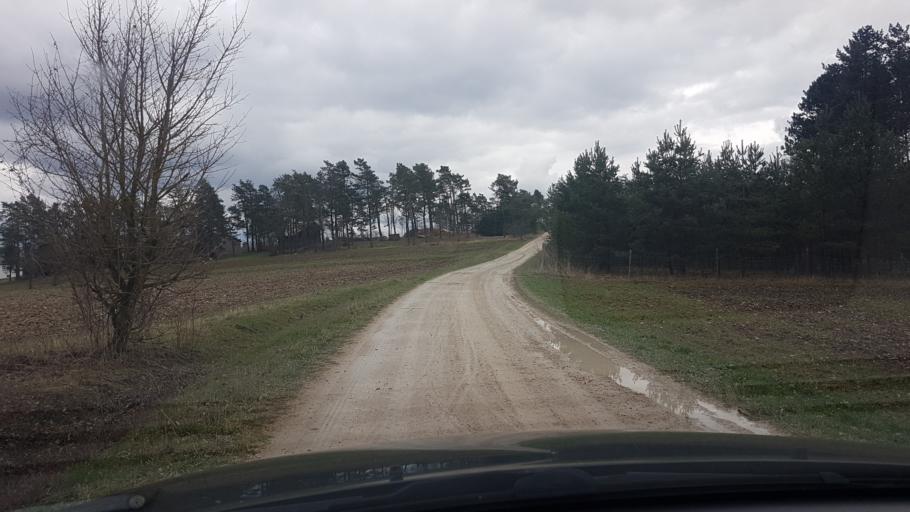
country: DE
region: Bavaria
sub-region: Upper Franconia
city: Poxdorf
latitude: 49.8734
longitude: 11.0871
